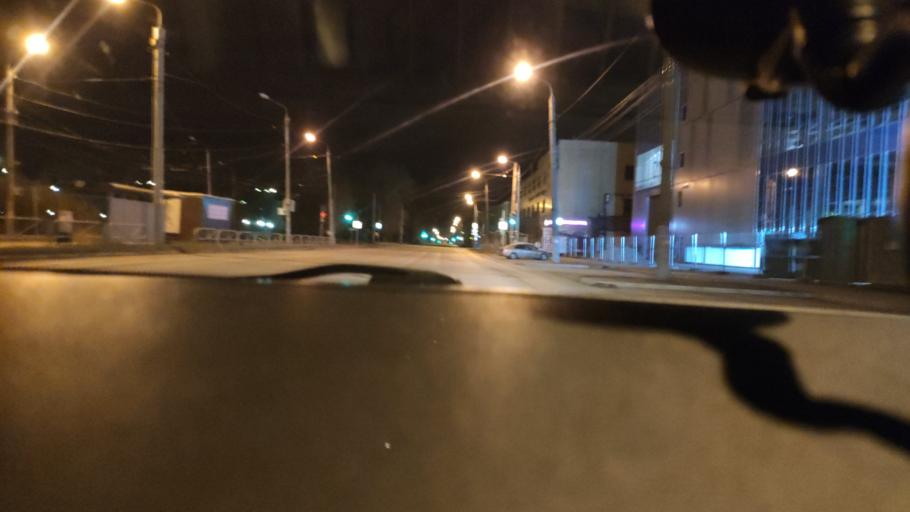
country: RU
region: Perm
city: Perm
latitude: 57.9657
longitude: 56.2445
